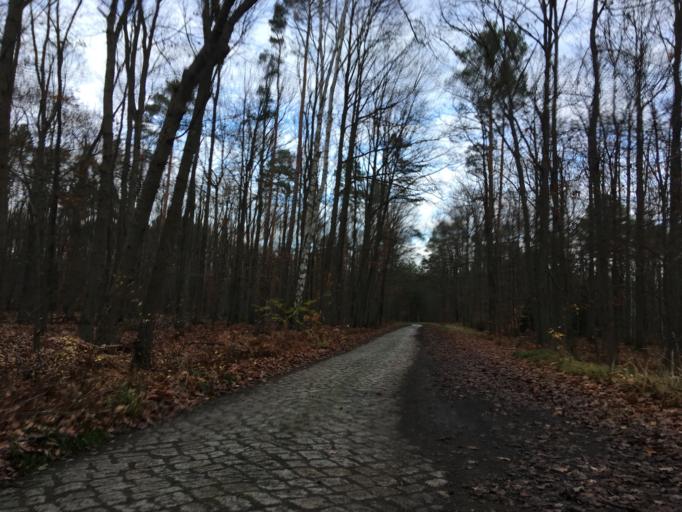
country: DE
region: Brandenburg
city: Tauer
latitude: 51.9439
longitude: 14.5153
